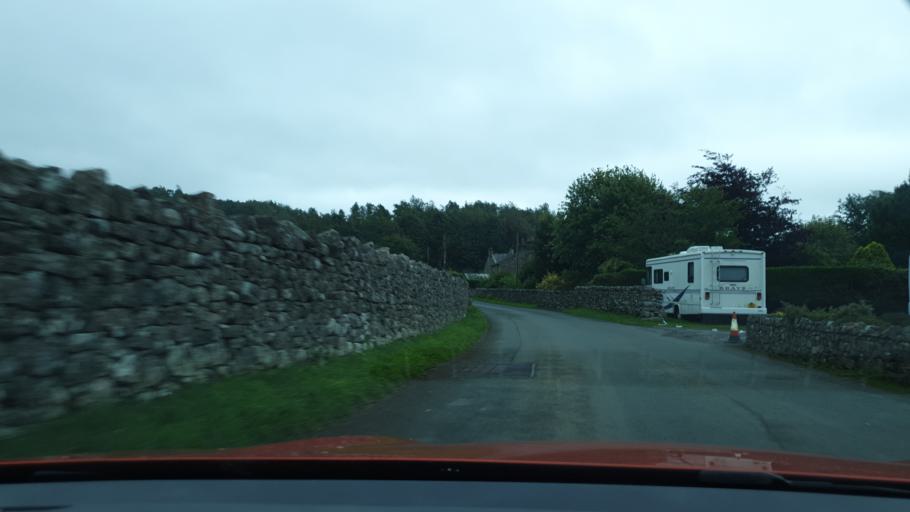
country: GB
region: England
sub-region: Cumbria
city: Seascale
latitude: 54.3901
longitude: -3.3346
